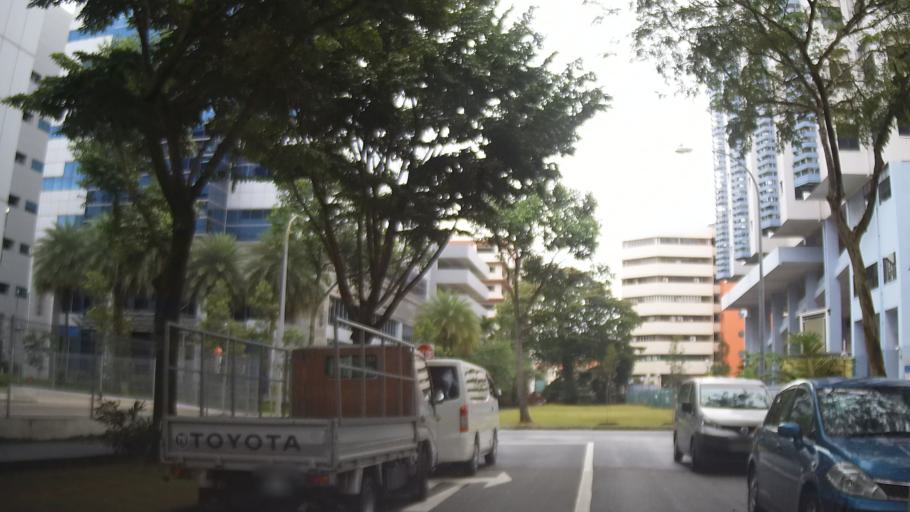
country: SG
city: Singapore
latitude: 1.3289
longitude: 103.8773
